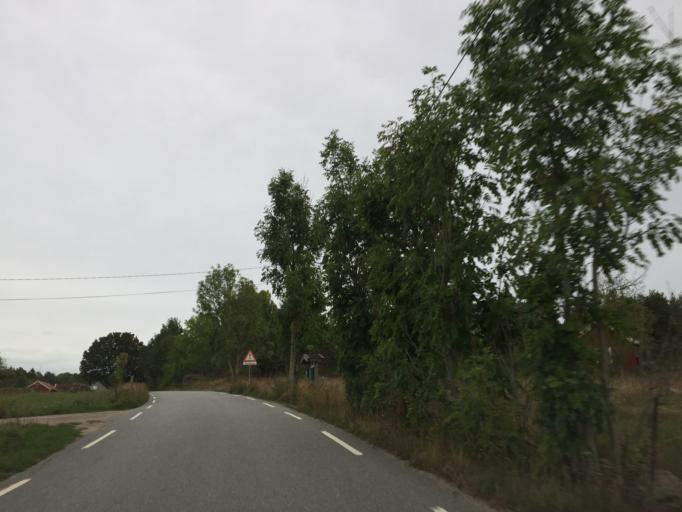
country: NO
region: Ostfold
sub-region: Hvaler
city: Skjaerhalden
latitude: 59.0717
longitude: 11.0046
